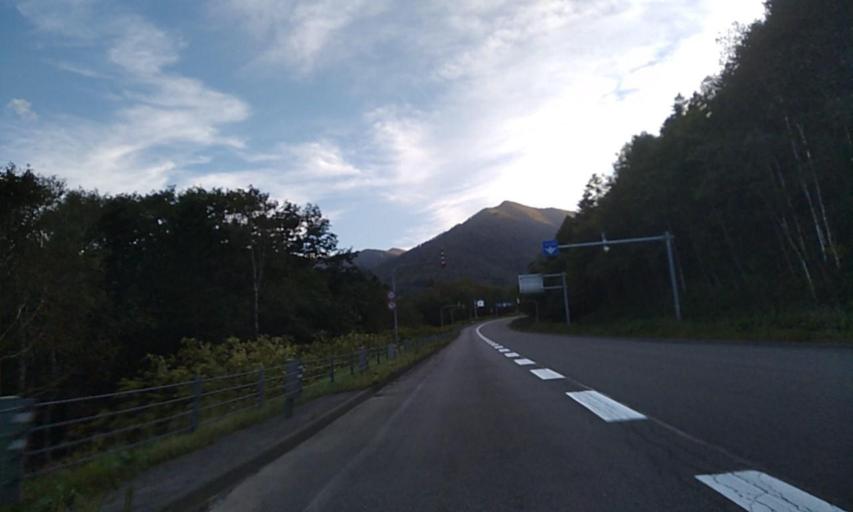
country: JP
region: Hokkaido
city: Otofuke
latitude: 42.9658
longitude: 142.8006
